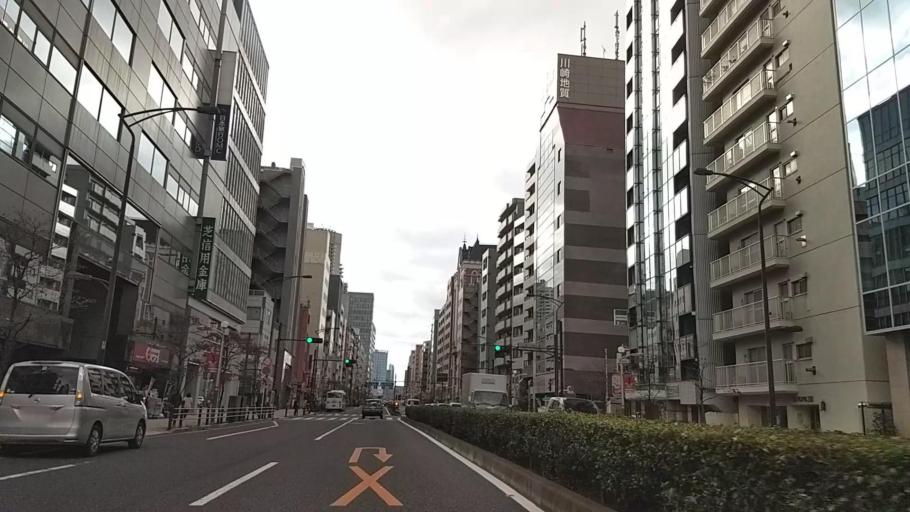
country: JP
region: Tokyo
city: Tokyo
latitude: 35.6509
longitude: 139.7449
